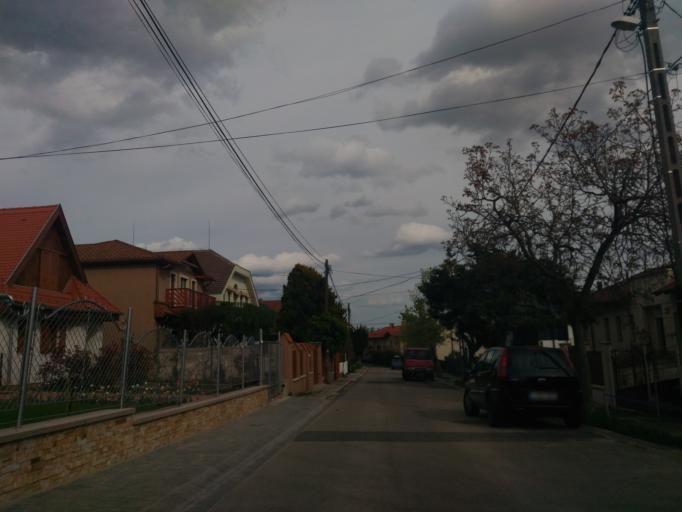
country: HU
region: Budapest
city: Budapest XXII. keruelet
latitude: 47.4280
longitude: 19.0274
